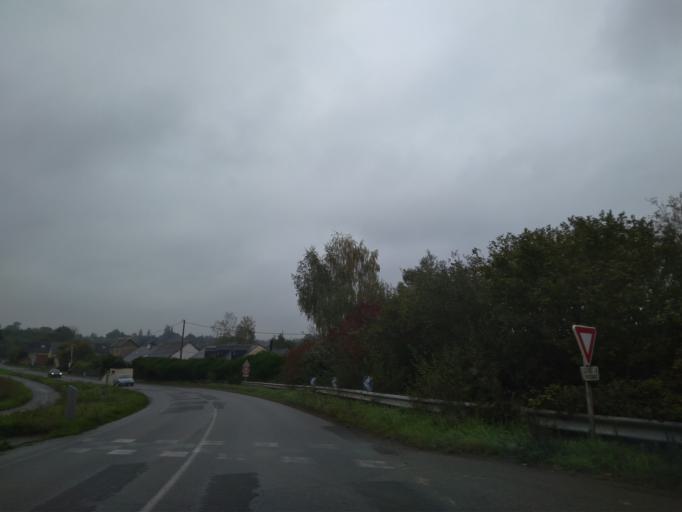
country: FR
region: Brittany
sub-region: Departement d'Ille-et-Vilaine
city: Saint-Gregoire
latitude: 48.1488
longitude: -1.6716
